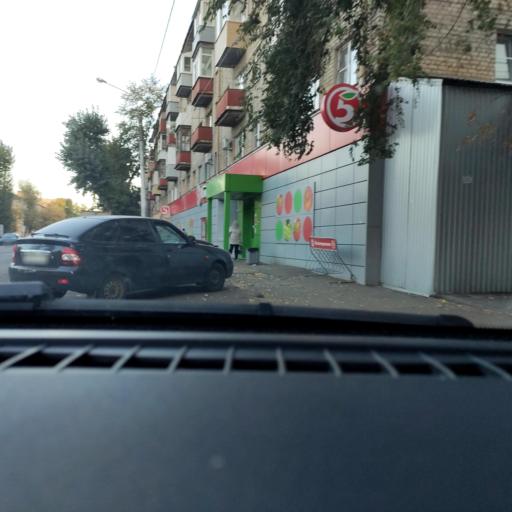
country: RU
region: Voronezj
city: Maslovka
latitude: 51.6204
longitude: 39.2460
